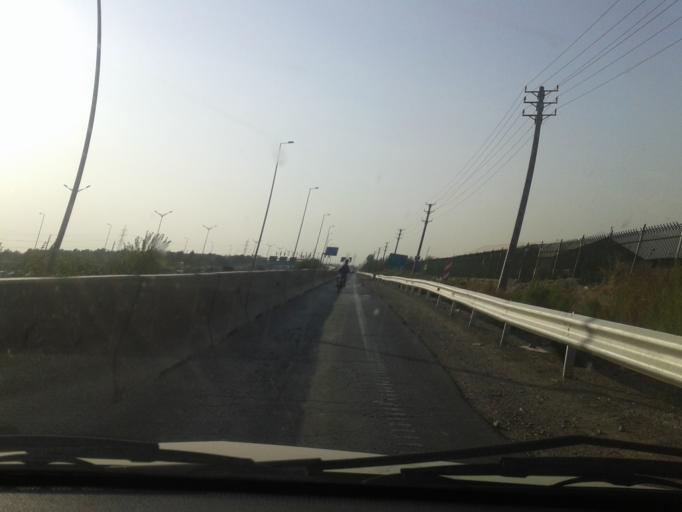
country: IR
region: Tehran
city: Eslamshahr
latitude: 35.6580
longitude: 51.2539
